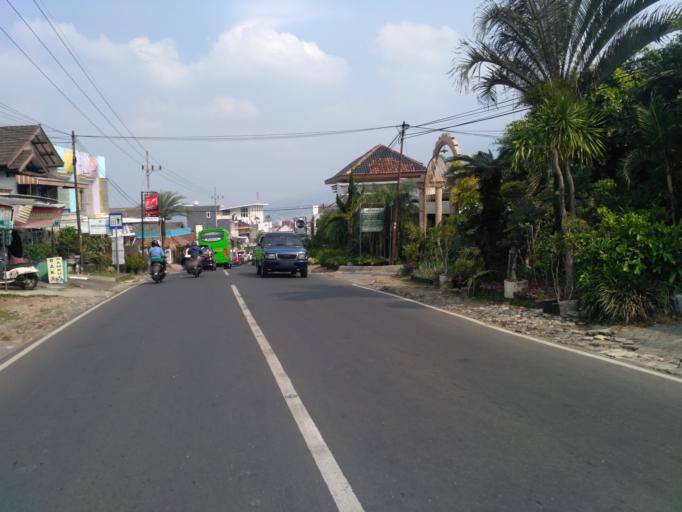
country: ID
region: East Java
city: Batu
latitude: -7.8468
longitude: 112.5283
